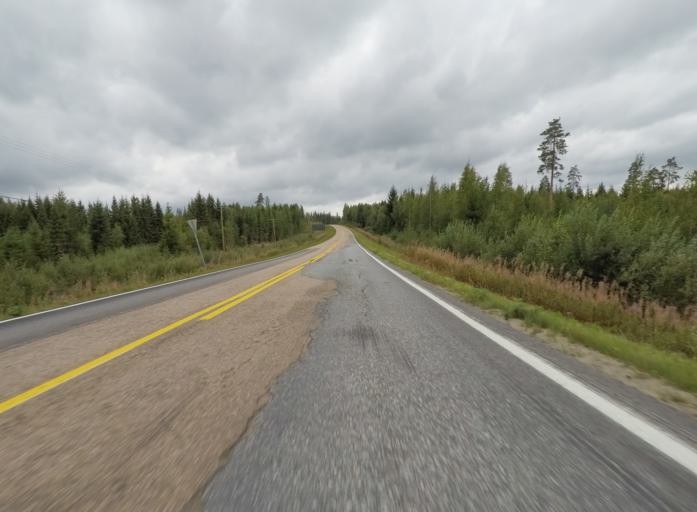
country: FI
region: Central Finland
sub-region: Jyvaeskylae
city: Hankasalmi
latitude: 62.3579
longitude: 26.5653
